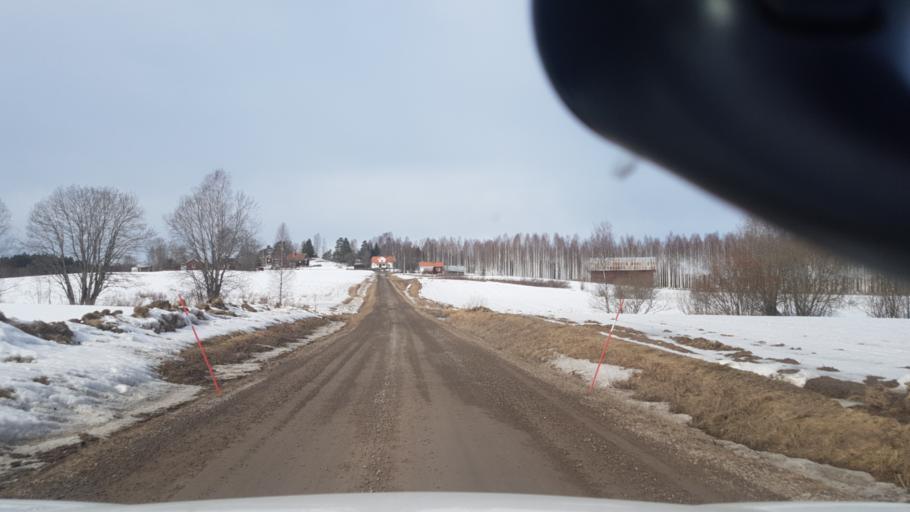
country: SE
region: Vaermland
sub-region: Eda Kommun
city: Charlottenberg
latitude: 59.8461
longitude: 12.3488
